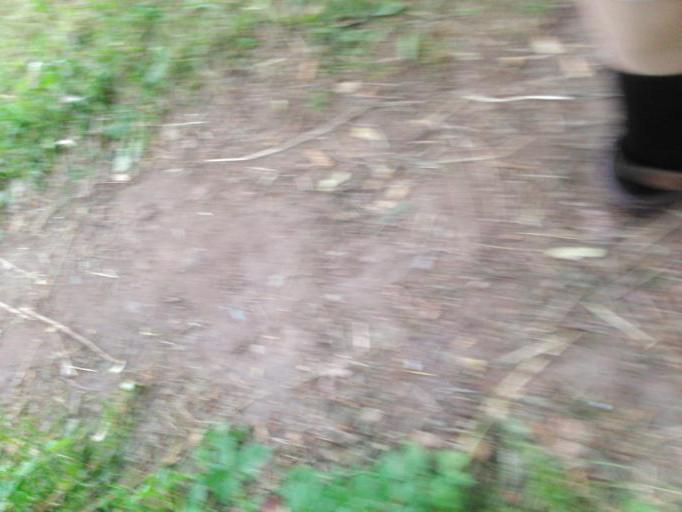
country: RU
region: St.-Petersburg
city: Pavlovsk
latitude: 59.6857
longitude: 30.4485
